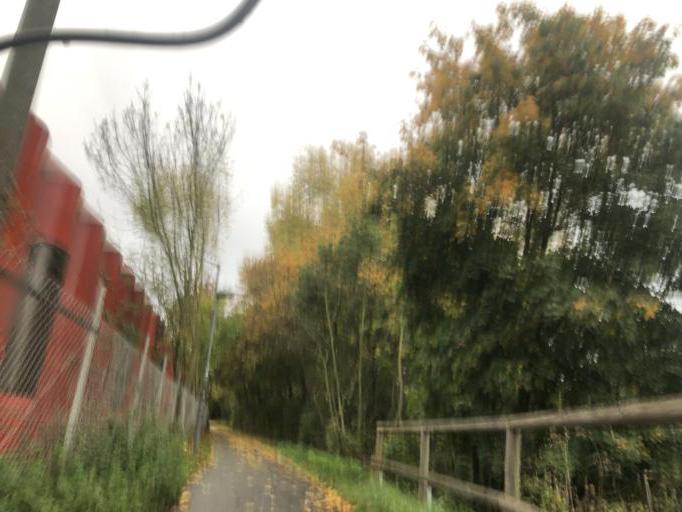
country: DE
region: Bavaria
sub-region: Regierungsbezirk Mittelfranken
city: Furth
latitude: 49.4882
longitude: 10.9869
